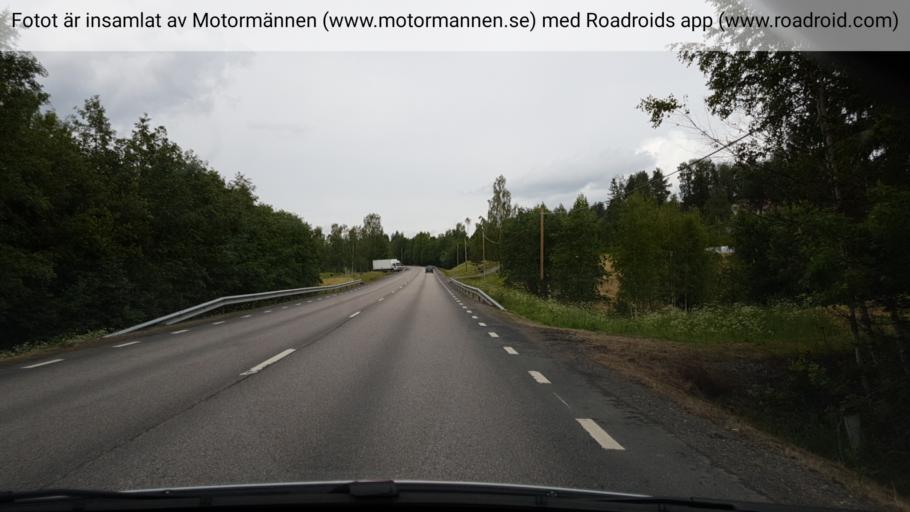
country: SE
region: Vaesternorrland
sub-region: Solleftea Kommun
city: Solleftea
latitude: 63.1887
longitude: 17.2444
